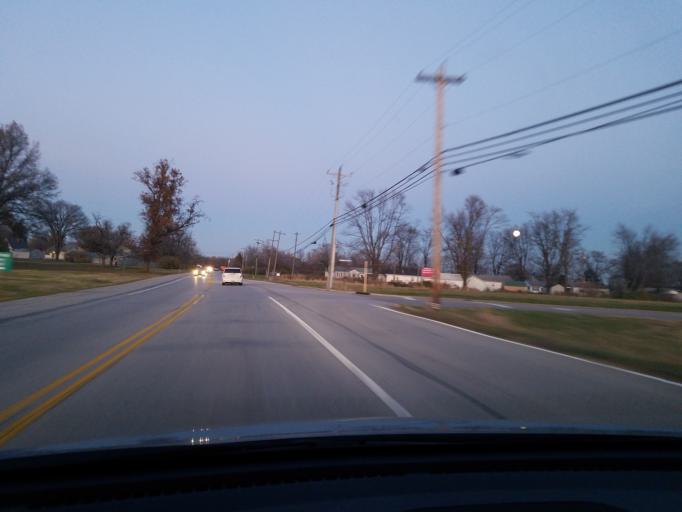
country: US
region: Indiana
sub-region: Clark County
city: Sellersburg
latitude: 38.4085
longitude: -85.7483
